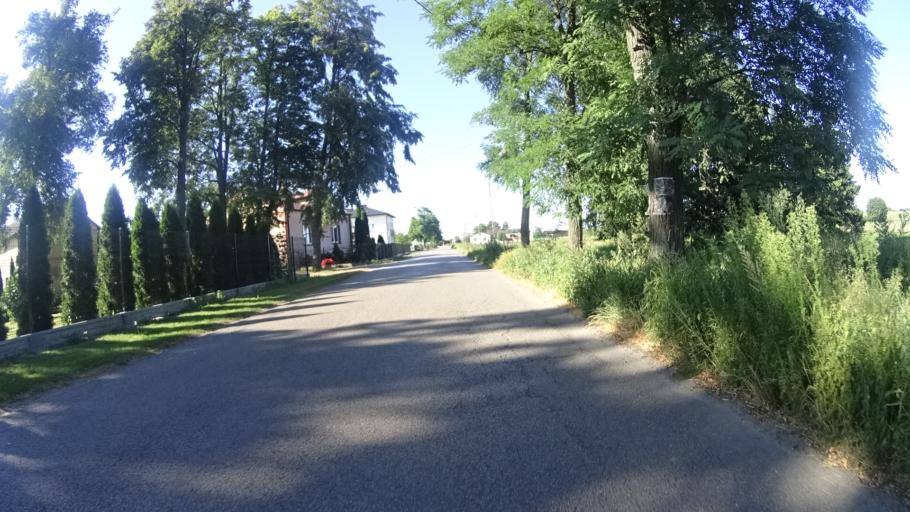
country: PL
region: Masovian Voivodeship
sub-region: Powiat bialobrzeski
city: Wysmierzyce
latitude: 51.6718
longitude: 20.8311
